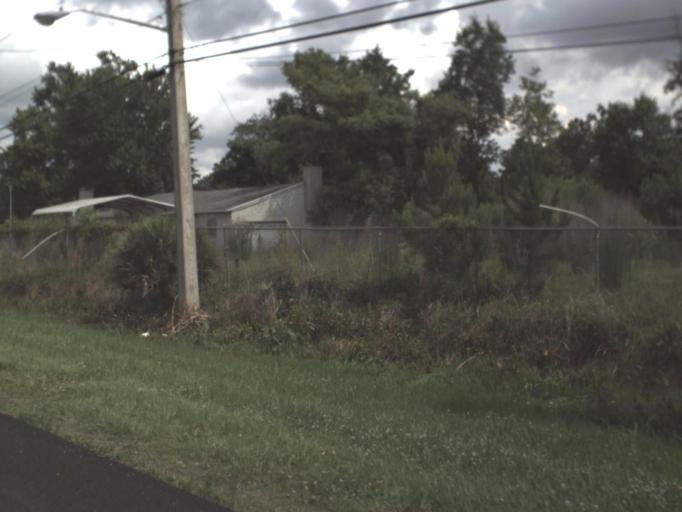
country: US
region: Florida
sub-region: Nassau County
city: Nassau Village-Ratliff
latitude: 30.4240
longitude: -81.7546
